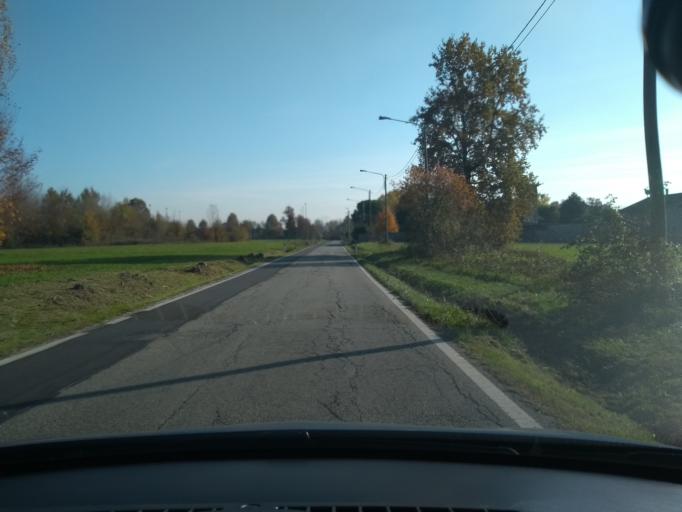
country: IT
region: Piedmont
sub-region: Provincia di Torino
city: Robassomero
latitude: 45.2059
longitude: 7.5558
